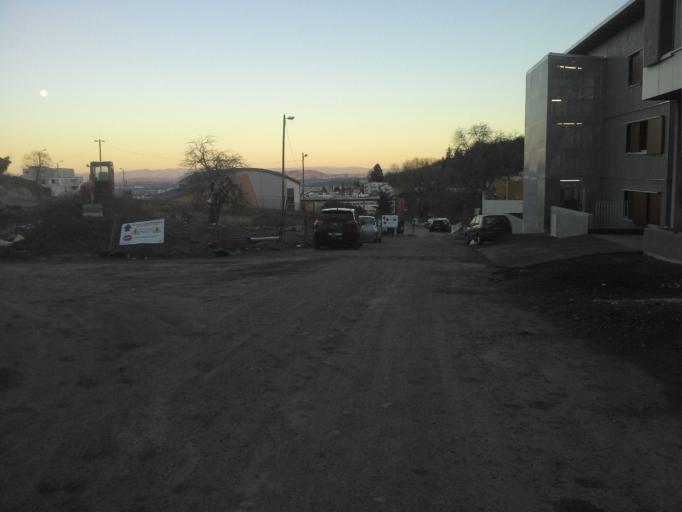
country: FR
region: Auvergne
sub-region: Departement du Puy-de-Dome
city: Durtol
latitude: 45.7929
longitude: 3.0655
